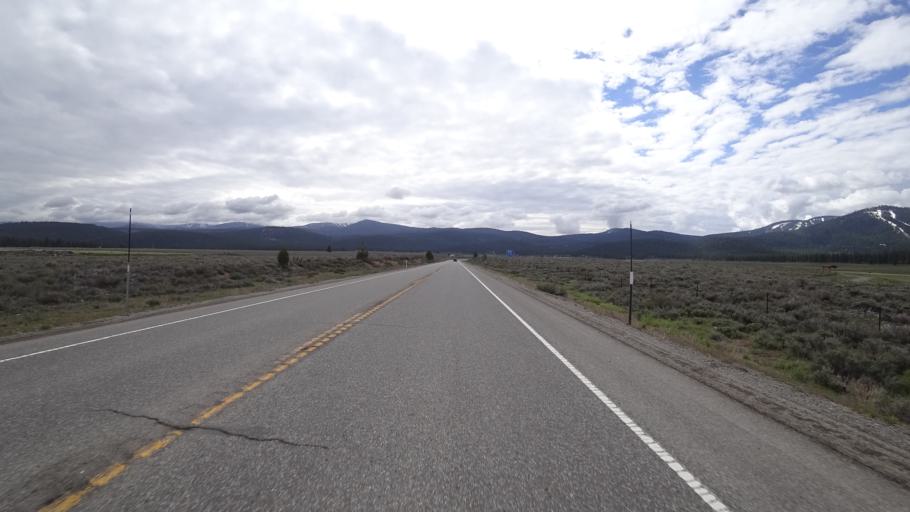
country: US
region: California
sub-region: Nevada County
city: Truckee
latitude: 39.3130
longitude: -120.1448
